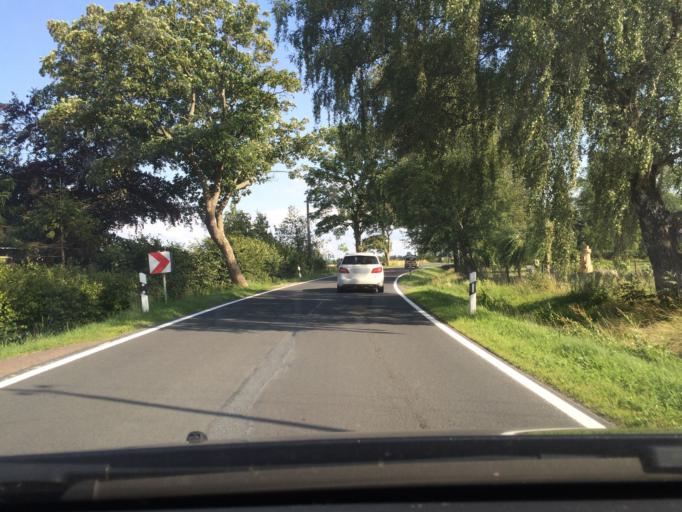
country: DE
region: Mecklenburg-Vorpommern
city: Niepars
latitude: 54.3348
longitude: 12.9318
